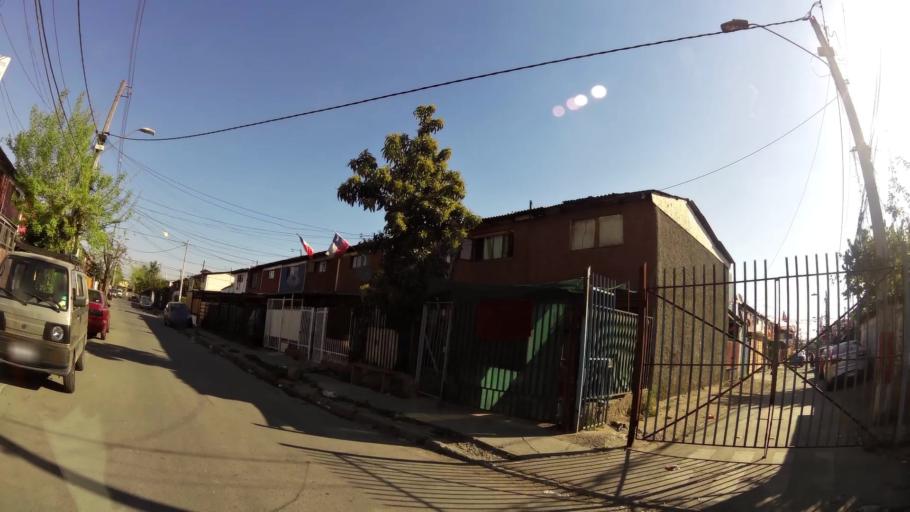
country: CL
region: Santiago Metropolitan
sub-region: Provincia de Santiago
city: La Pintana
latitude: -33.5604
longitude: -70.6094
